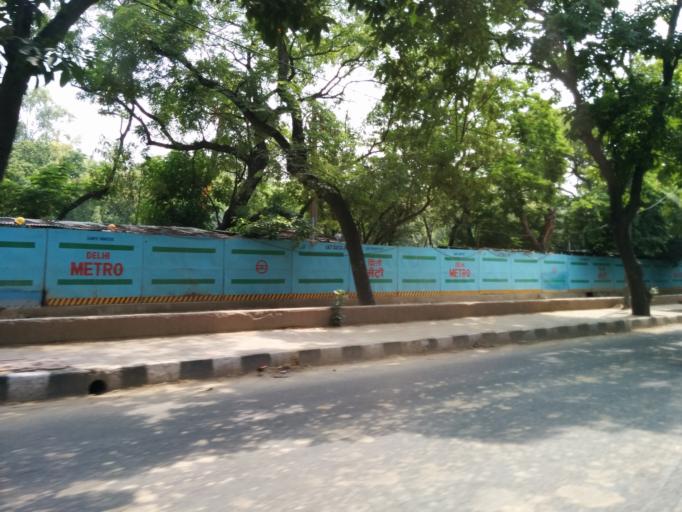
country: IN
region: NCT
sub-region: New Delhi
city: New Delhi
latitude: 28.5469
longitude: 77.1936
